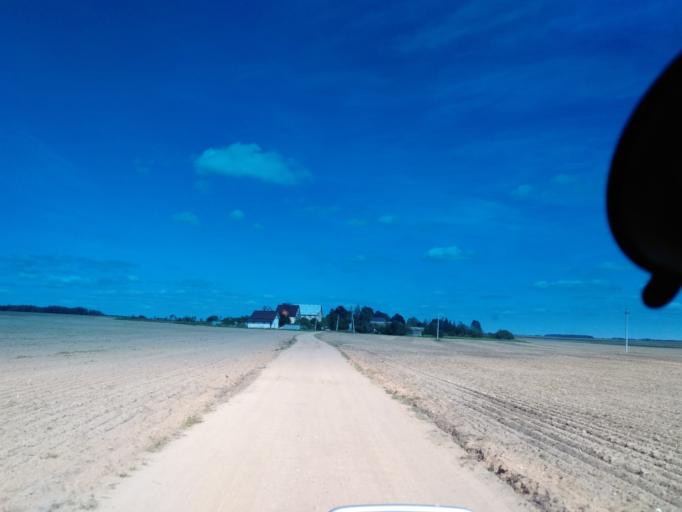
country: BY
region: Minsk
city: Stan'kava
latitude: 53.6369
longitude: 27.3074
